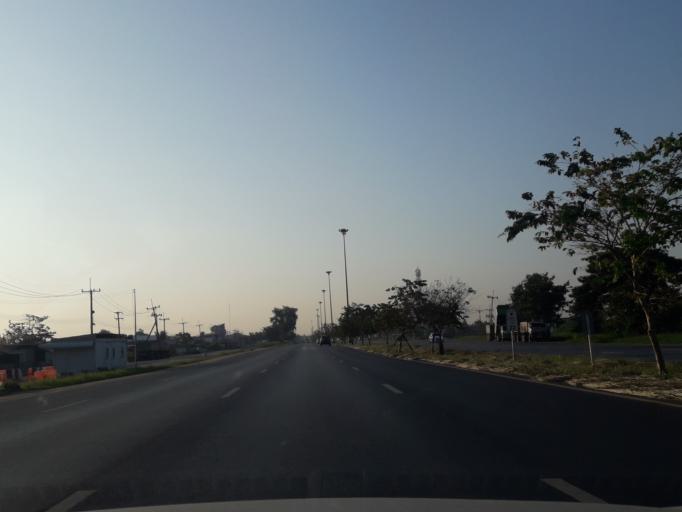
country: TH
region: Phra Nakhon Si Ayutthaya
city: Bang Pa-in
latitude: 14.2017
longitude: 100.5495
